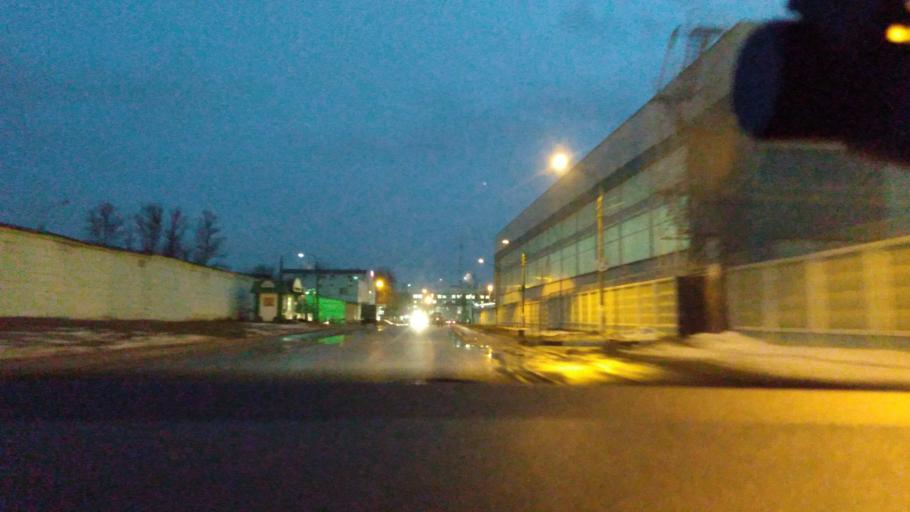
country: RU
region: Moskovskaya
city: Saltykovka
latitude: 55.7962
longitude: 37.9239
